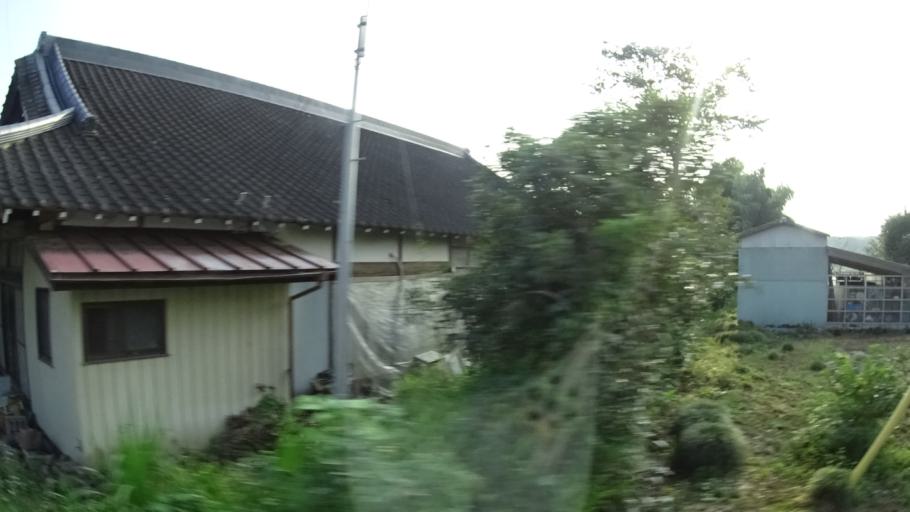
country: JP
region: Tochigi
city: Karasuyama
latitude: 36.5688
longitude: 140.1036
